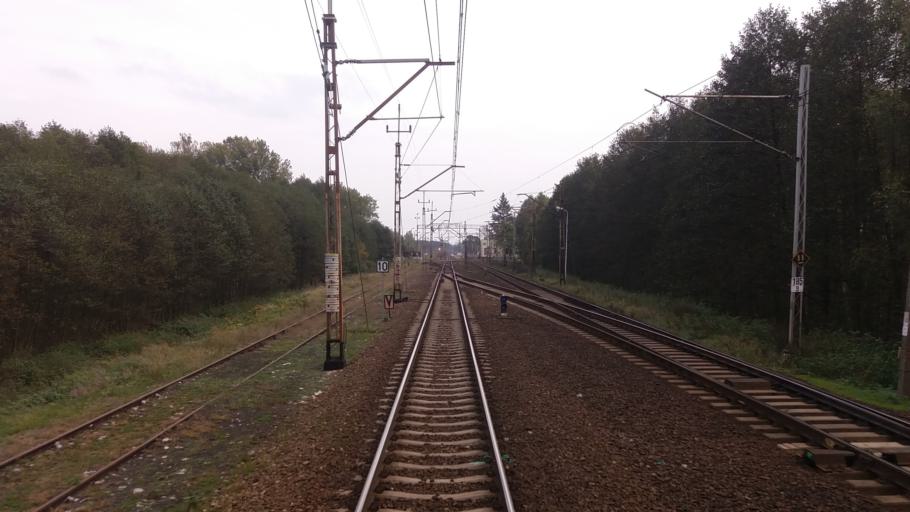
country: PL
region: West Pomeranian Voivodeship
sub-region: Powiat stargardzki
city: Kobylanka
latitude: 53.3732
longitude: 14.8568
